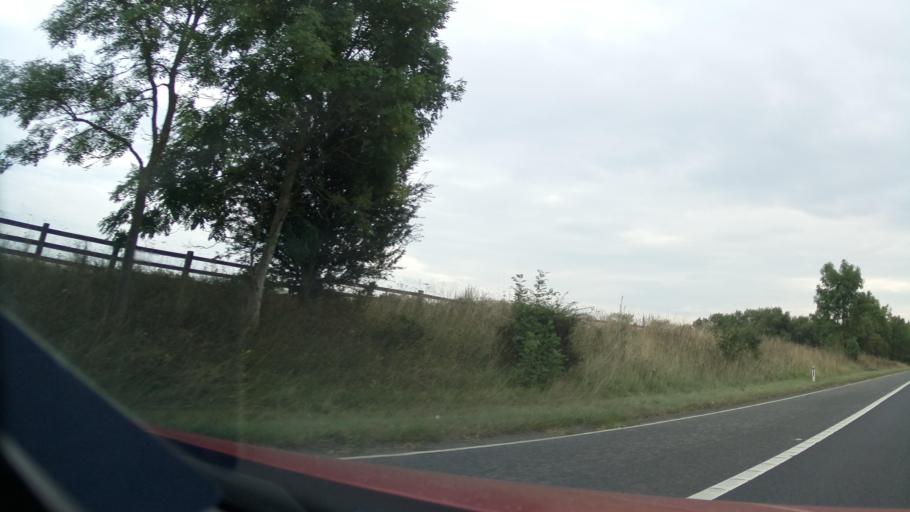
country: GB
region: England
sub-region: Darlington
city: Coatham Mundeville
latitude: 54.5769
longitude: -1.5699
